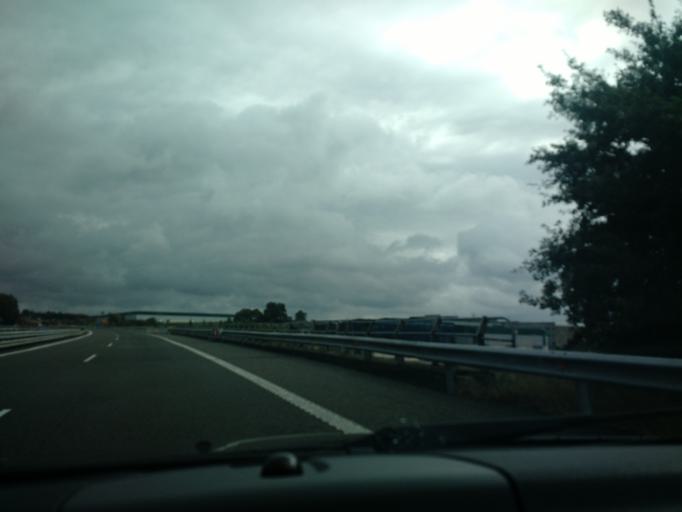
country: ES
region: Galicia
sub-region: Provincia da Coruna
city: Oroso
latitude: 42.9749
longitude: -8.4433
